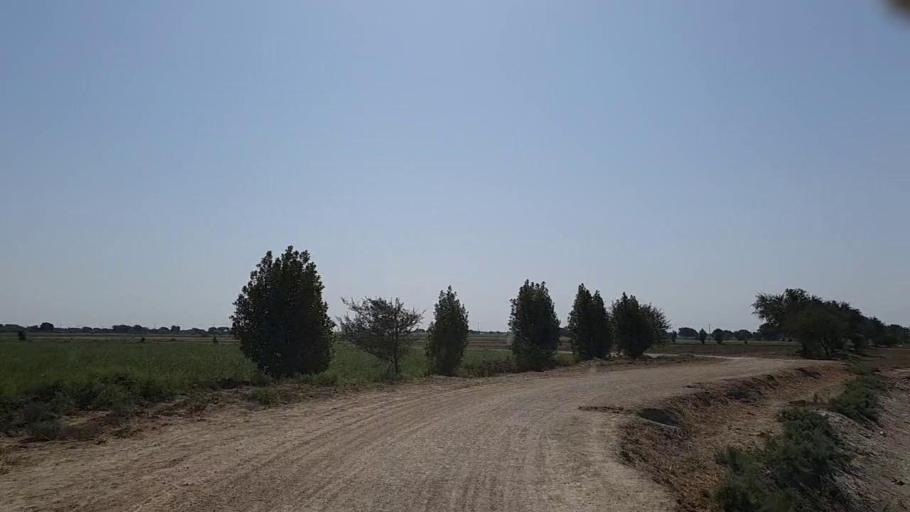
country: PK
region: Sindh
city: Mirpur Batoro
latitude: 24.6819
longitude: 68.2887
